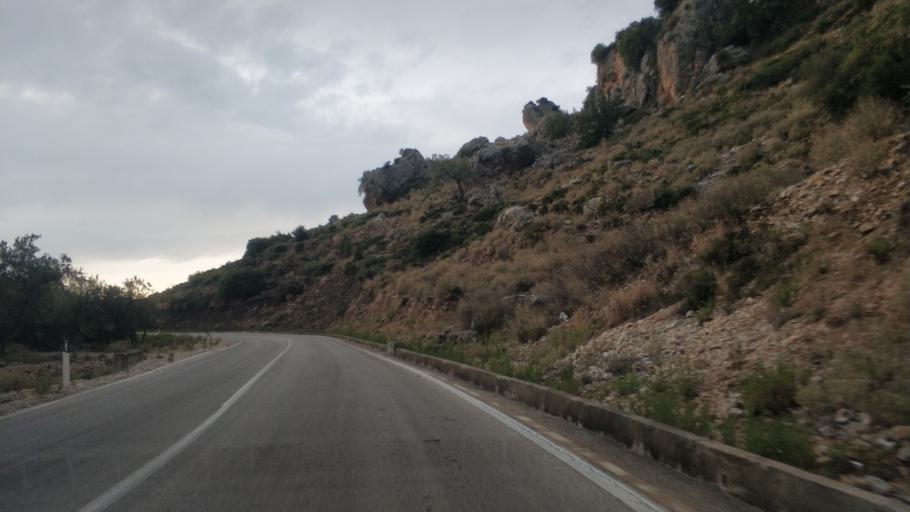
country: AL
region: Vlore
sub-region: Rrethi i Sarandes
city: Lukove
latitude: 40.0349
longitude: 19.8856
